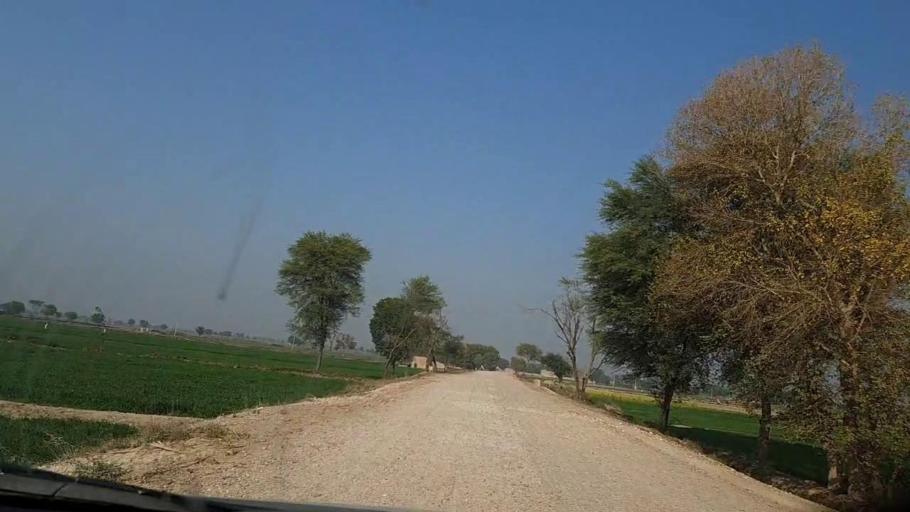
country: PK
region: Sindh
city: Moro
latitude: 26.7741
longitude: 67.9331
